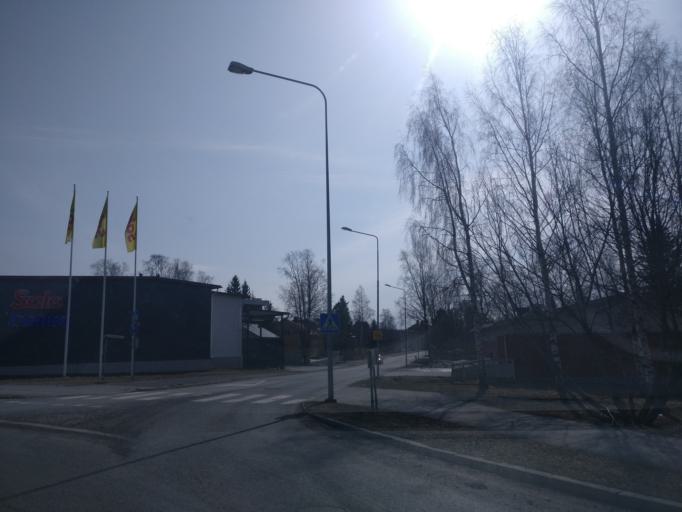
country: FI
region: Lapland
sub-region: Kemi-Tornio
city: Kemi
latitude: 65.7298
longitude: 24.5995
